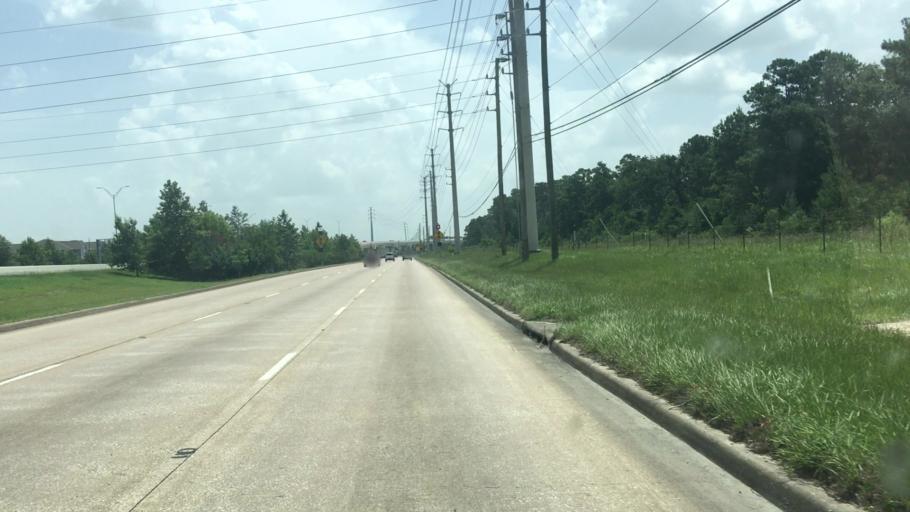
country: US
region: Texas
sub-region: Harris County
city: Atascocita
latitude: 29.9338
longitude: -95.2171
